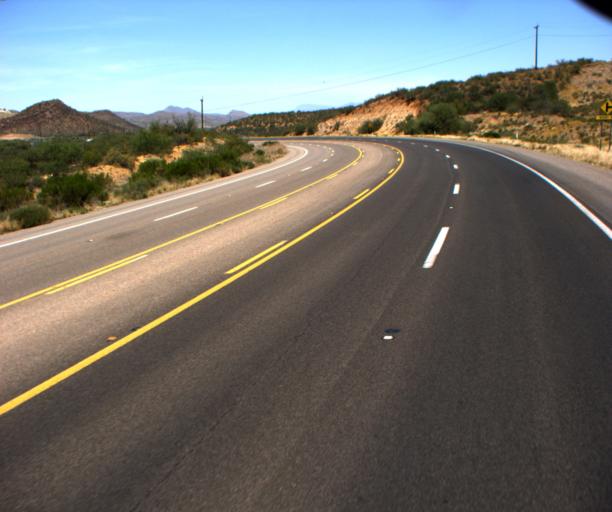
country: US
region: Arizona
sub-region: Gila County
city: Claypool
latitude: 33.4388
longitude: -110.8289
